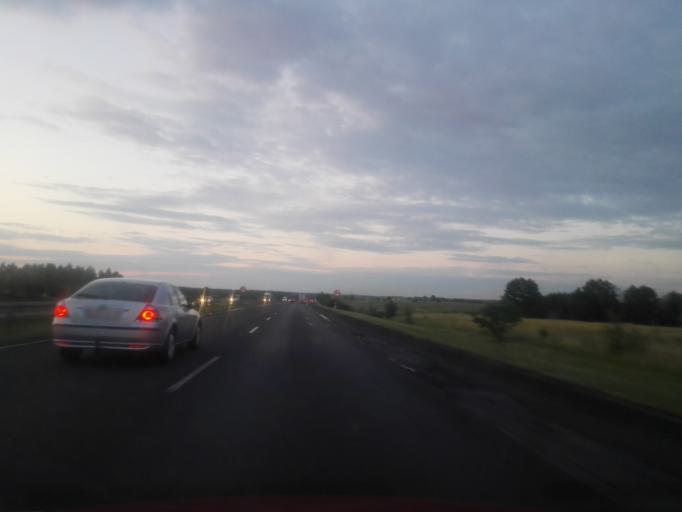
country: PL
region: Lodz Voivodeship
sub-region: Powiat radomszczanski
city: Kamiensk
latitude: 51.2042
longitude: 19.4800
